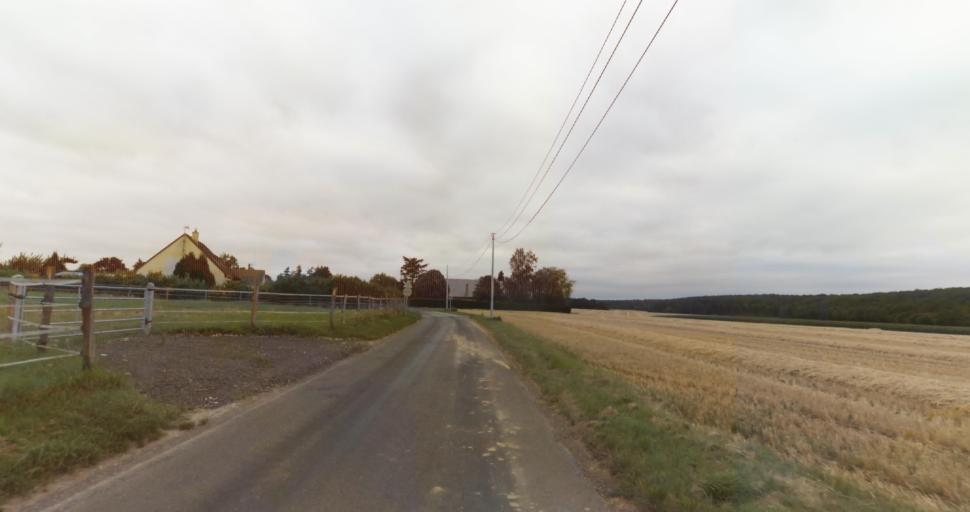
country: FR
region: Haute-Normandie
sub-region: Departement de l'Eure
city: Marcilly-sur-Eure
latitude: 48.8868
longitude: 1.3028
